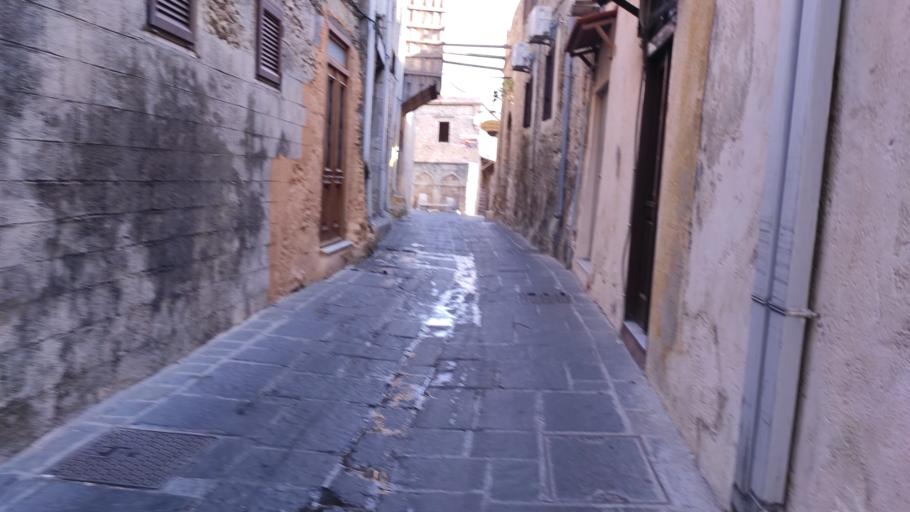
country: GR
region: South Aegean
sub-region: Nomos Dodekanisou
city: Rodos
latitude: 36.4406
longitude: 28.2282
